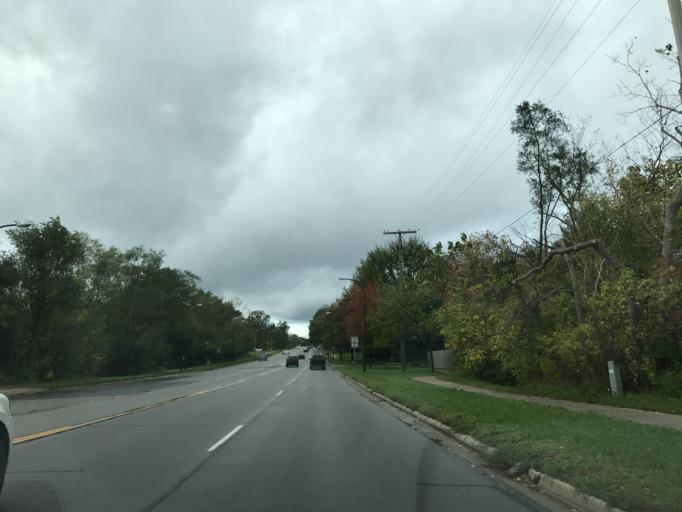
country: US
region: Michigan
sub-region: Washtenaw County
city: Ann Arbor
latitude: 42.2450
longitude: -83.7036
